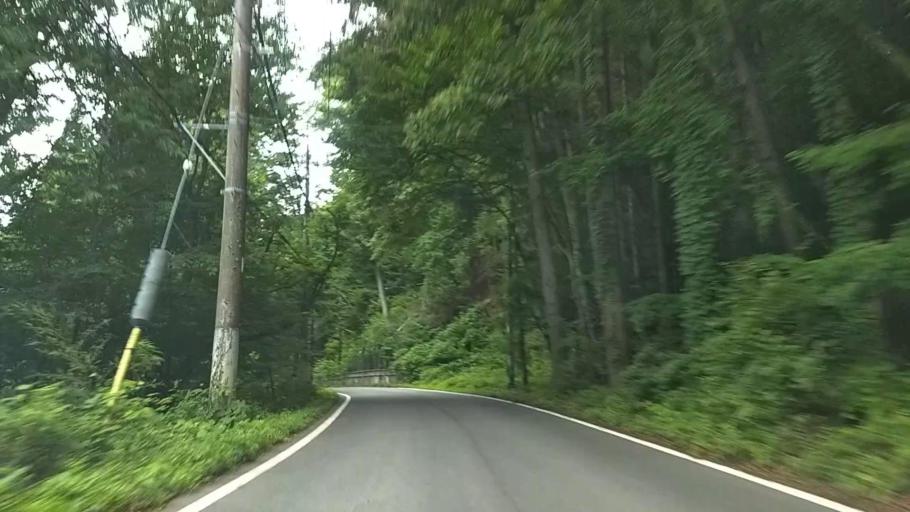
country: JP
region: Yamanashi
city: Fujikawaguchiko
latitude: 35.5172
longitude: 138.7399
